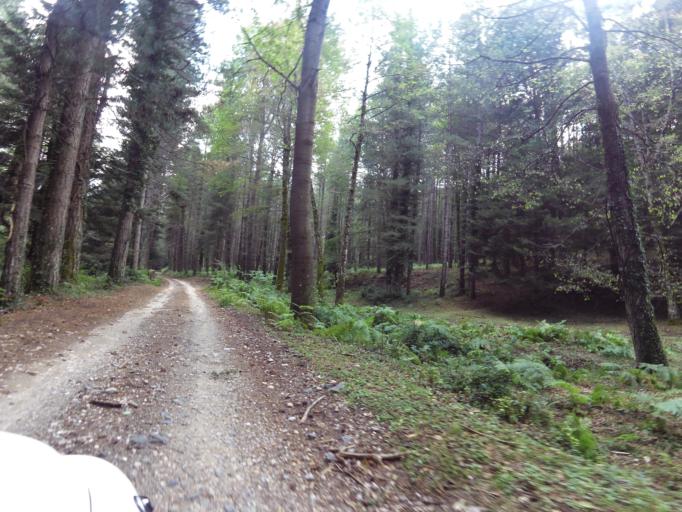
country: IT
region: Calabria
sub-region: Provincia di Vibo-Valentia
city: Nardodipace
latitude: 38.5172
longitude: 16.3794
